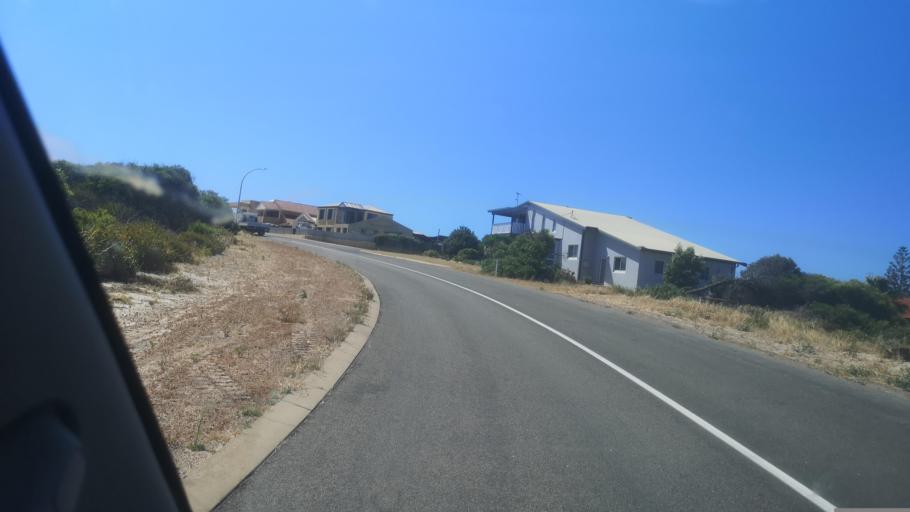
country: AU
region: Western Australia
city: Port Denison
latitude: -29.2810
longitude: 114.9221
